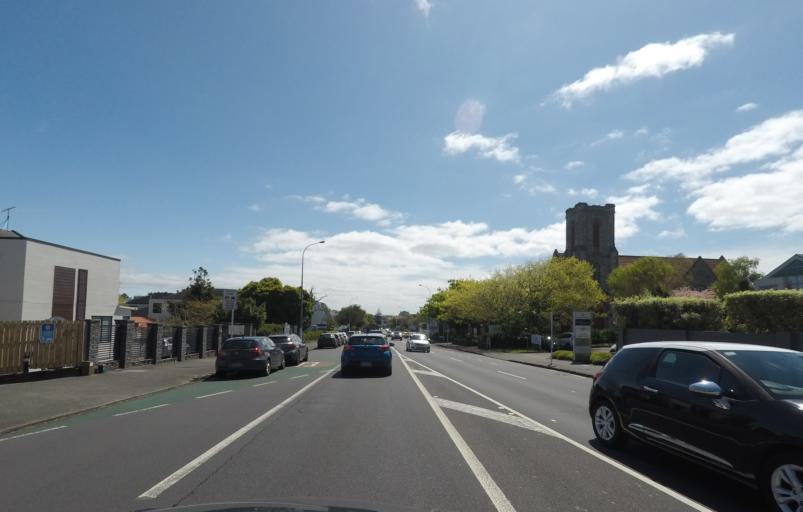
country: NZ
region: Auckland
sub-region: Auckland
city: Auckland
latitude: -36.8749
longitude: 174.7846
